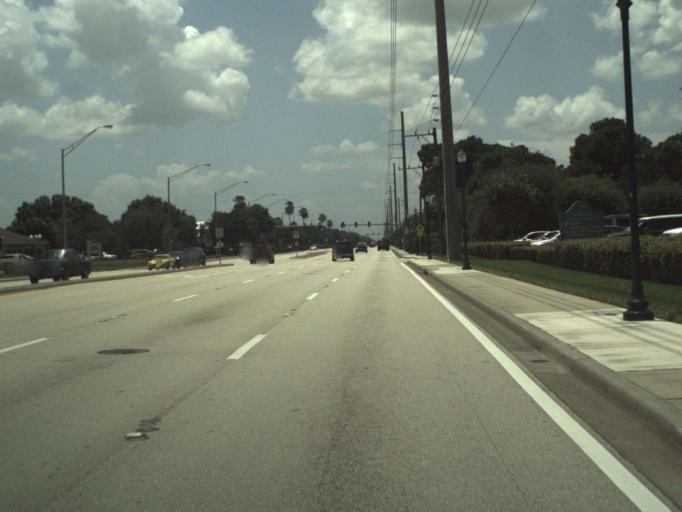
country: US
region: Florida
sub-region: Martin County
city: North River Shores
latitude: 27.2712
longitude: -80.2919
